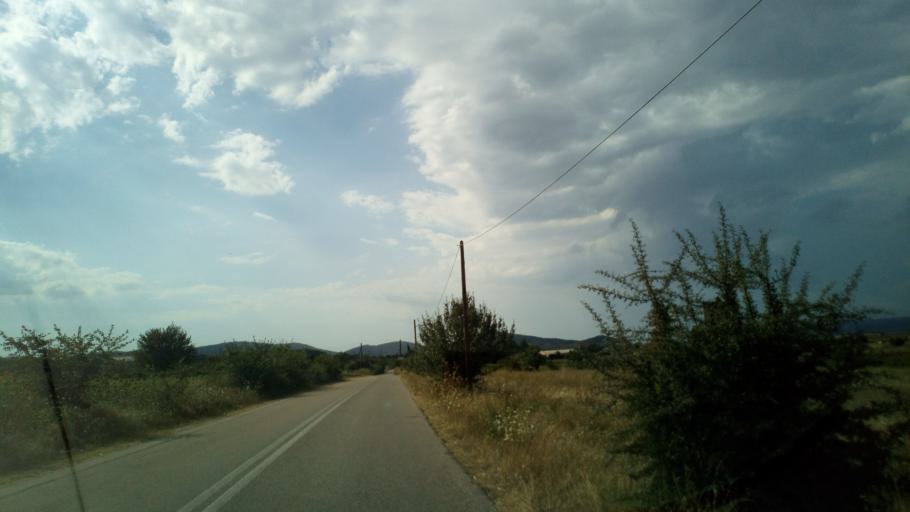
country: GR
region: Central Macedonia
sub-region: Nomos Chalkidikis
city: Galatista
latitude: 40.5085
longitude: 23.3727
